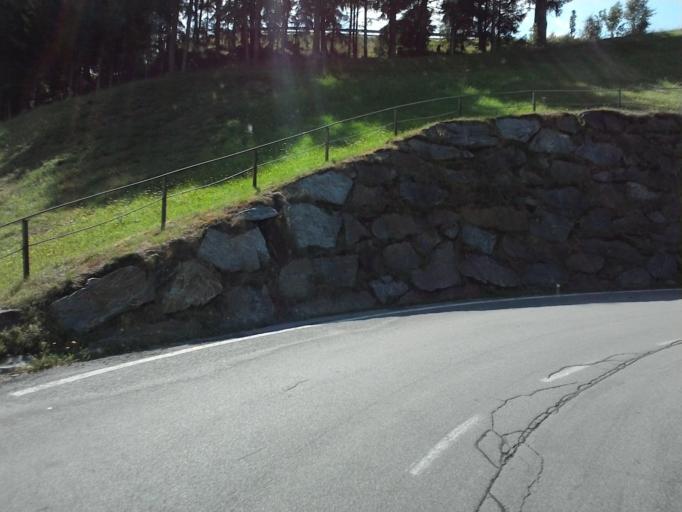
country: AT
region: Tyrol
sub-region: Politischer Bezirk Lienz
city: Strassen
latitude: 46.7411
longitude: 12.4710
